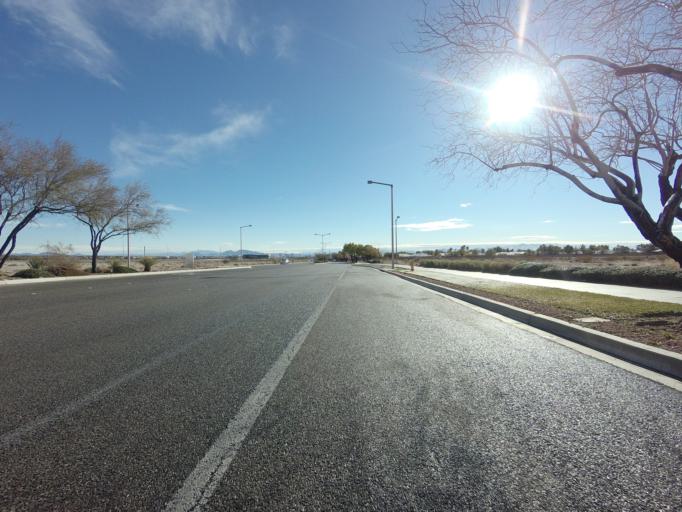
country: US
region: Nevada
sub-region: Clark County
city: Summerlin South
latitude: 36.1153
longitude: -115.3276
